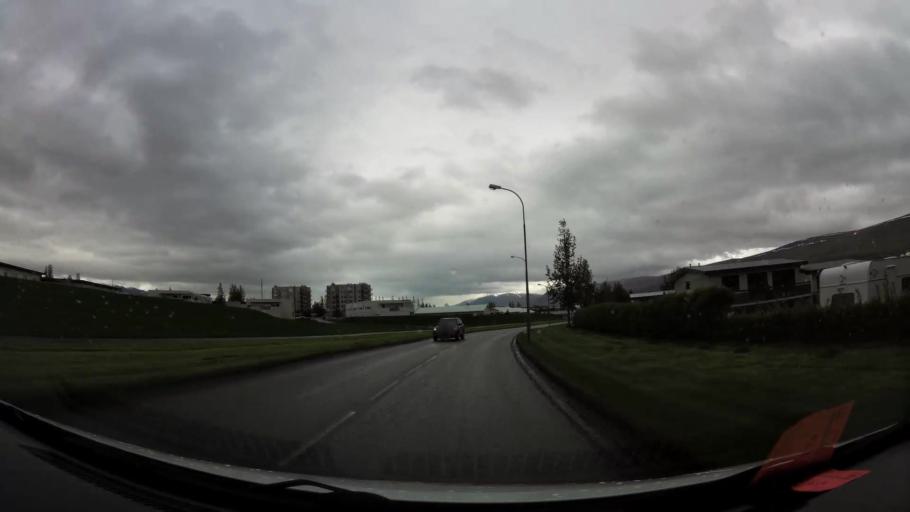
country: IS
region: Northeast
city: Akureyri
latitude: 65.6922
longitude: -18.1293
